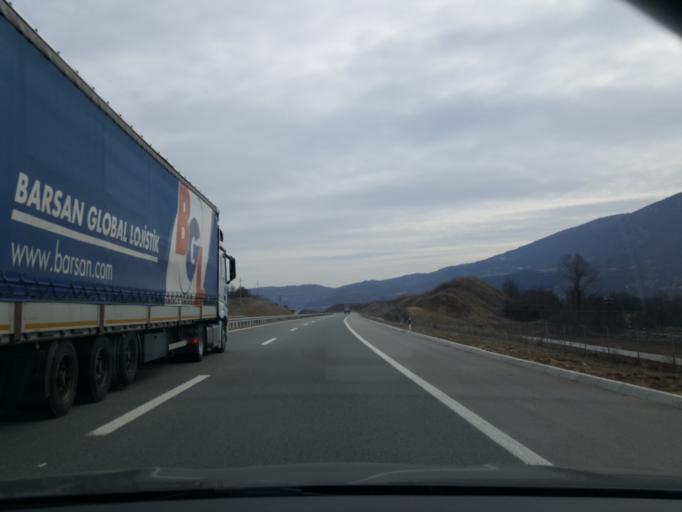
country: RS
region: Central Serbia
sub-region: Pirotski Okrug
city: Pirot
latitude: 43.2193
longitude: 22.4999
